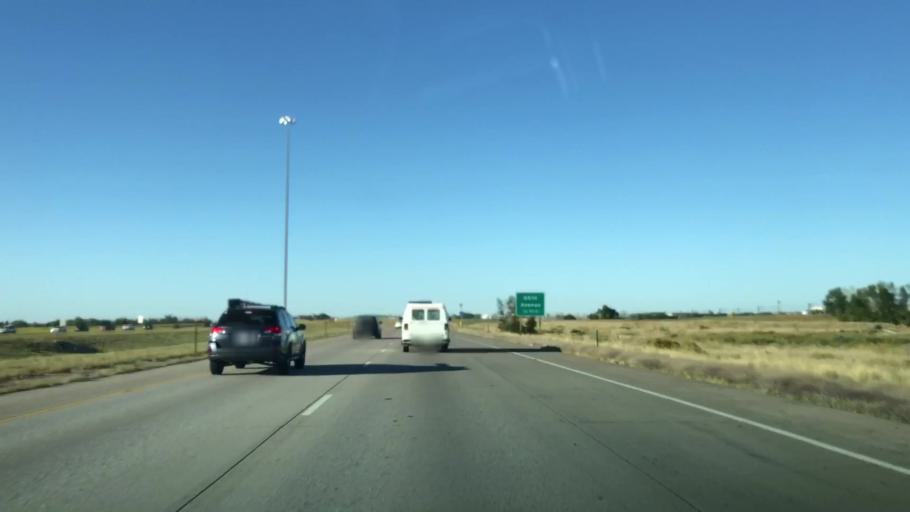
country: US
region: Colorado
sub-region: Adams County
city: Aurora
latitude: 39.7899
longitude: -104.7890
